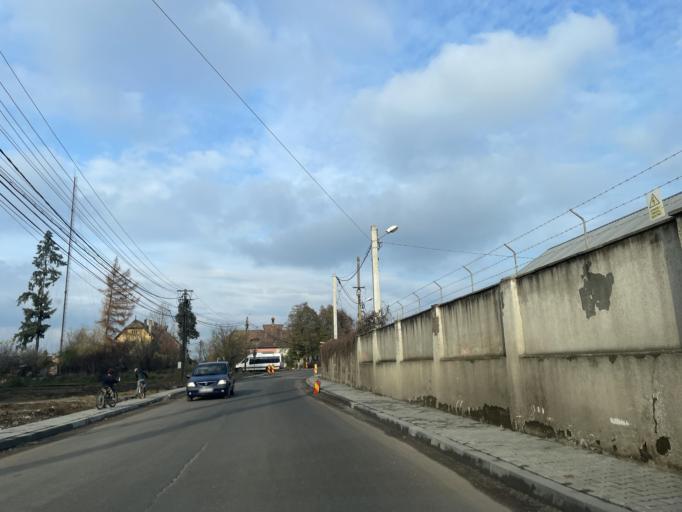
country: RO
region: Mures
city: Reghin-Sat
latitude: 46.7788
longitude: 24.7288
